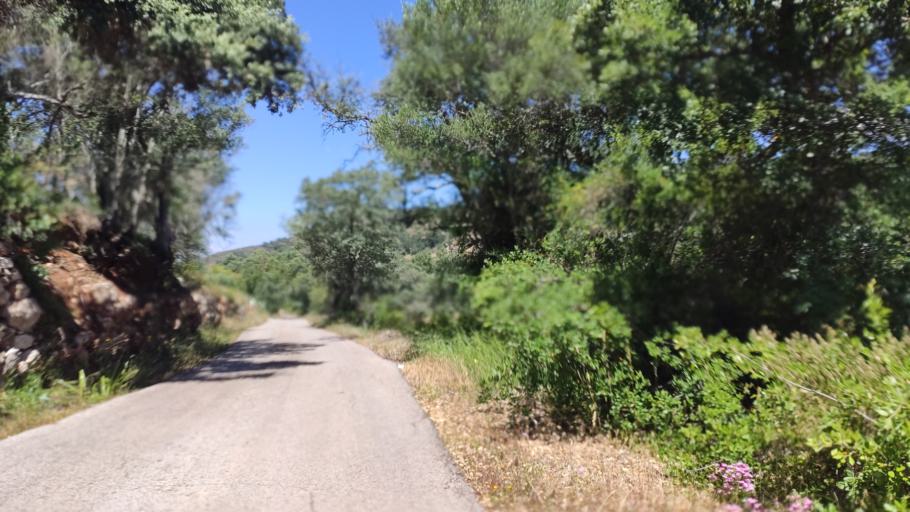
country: PT
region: Faro
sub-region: Sao Bras de Alportel
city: Sao Bras de Alportel
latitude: 37.1726
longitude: -7.9149
